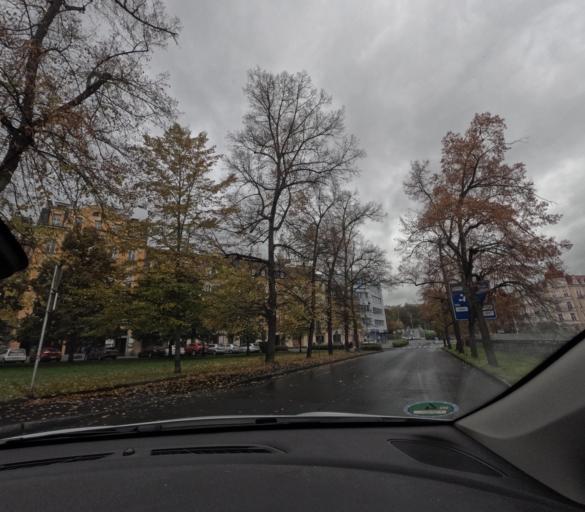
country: CZ
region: Karlovarsky
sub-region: Okres Karlovy Vary
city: Karlovy Vary
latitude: 50.2314
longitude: 12.8724
